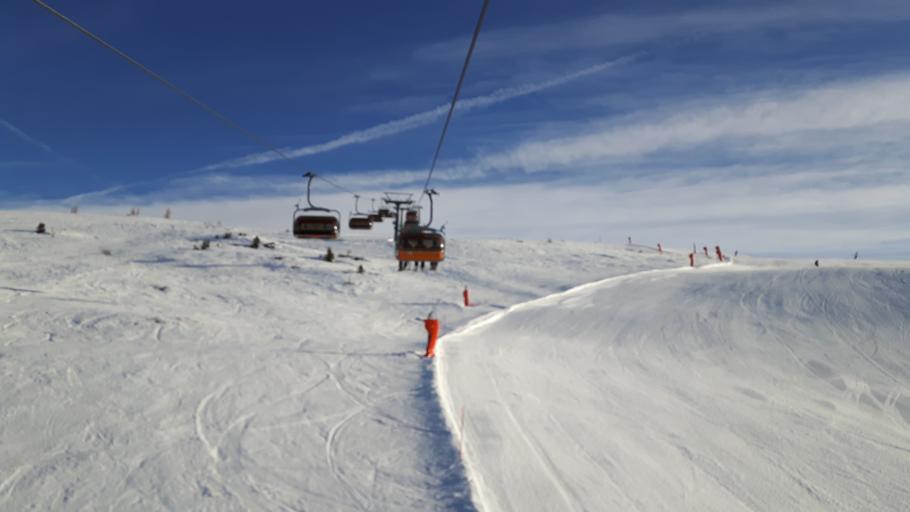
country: IT
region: Trentino-Alto Adige
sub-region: Provincia di Trento
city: Moena
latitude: 46.3399
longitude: 11.7135
